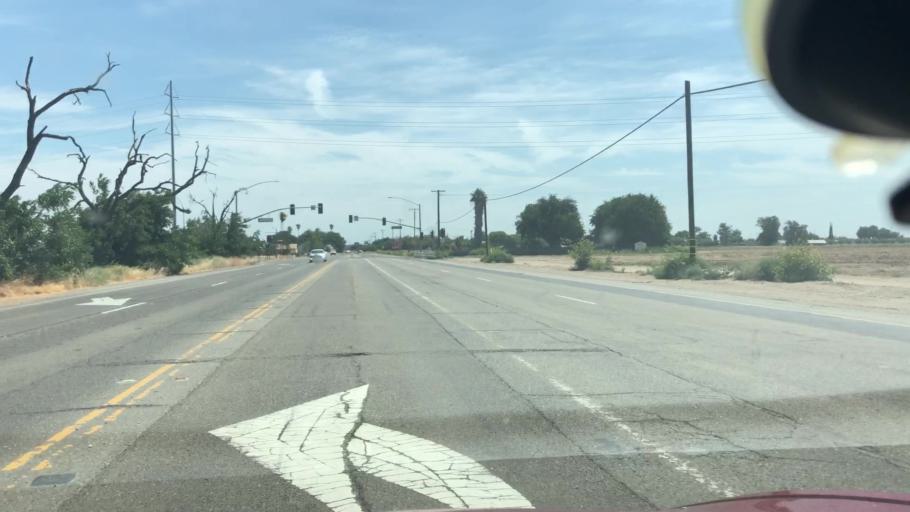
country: US
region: California
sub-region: San Joaquin County
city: Lathrop
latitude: 37.7947
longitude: -121.2797
